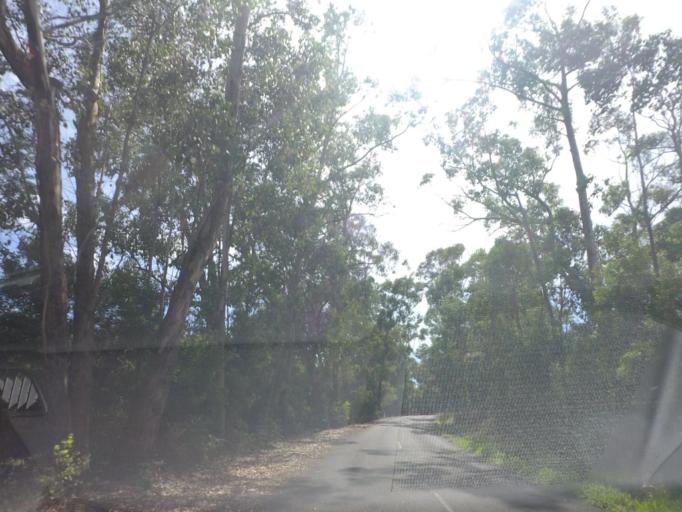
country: AU
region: Victoria
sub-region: Murrindindi
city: Kinglake West
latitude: -37.4585
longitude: 145.4019
